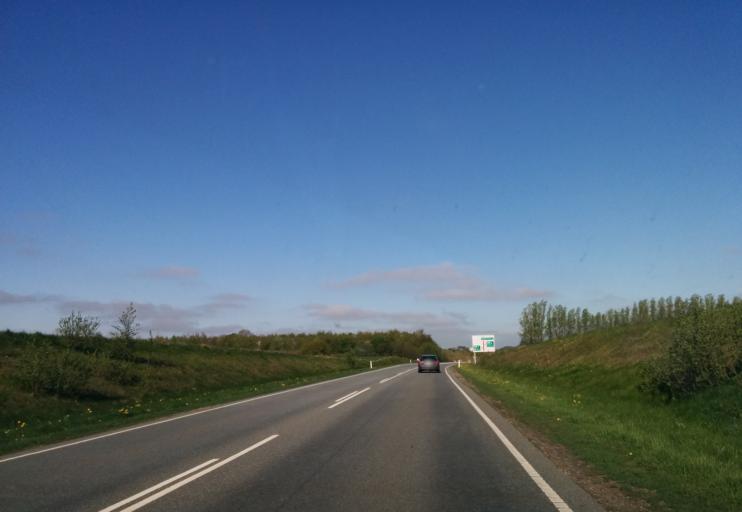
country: DK
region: Central Jutland
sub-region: Arhus Kommune
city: Kolt
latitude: 56.1190
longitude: 10.0897
